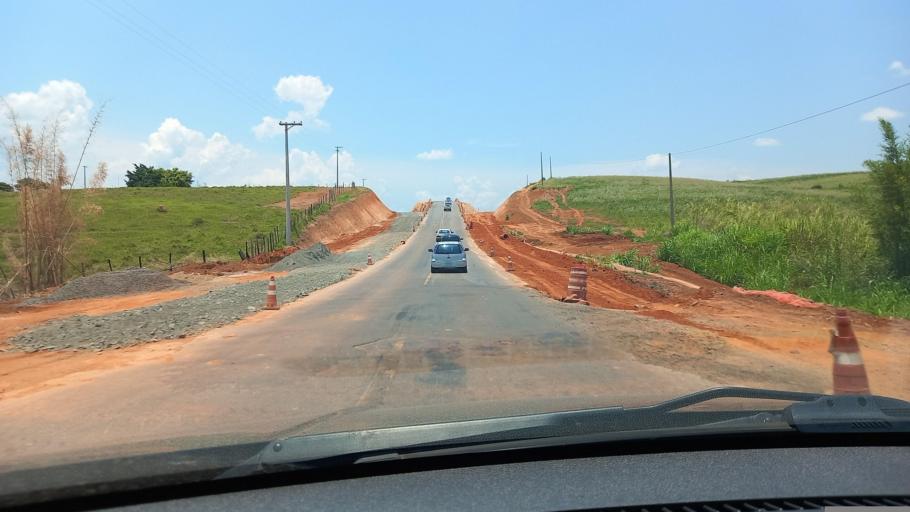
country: BR
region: Sao Paulo
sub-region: Itapira
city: Itapira
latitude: -22.3981
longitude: -46.8555
